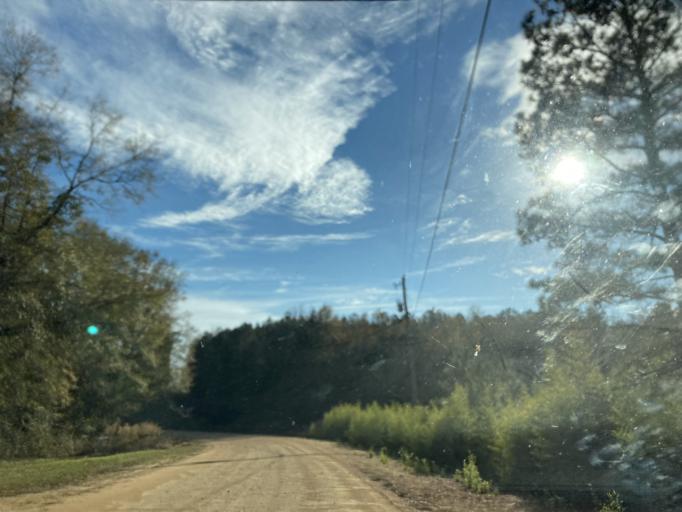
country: US
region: Georgia
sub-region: Jones County
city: Gray
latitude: 32.9070
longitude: -83.4908
